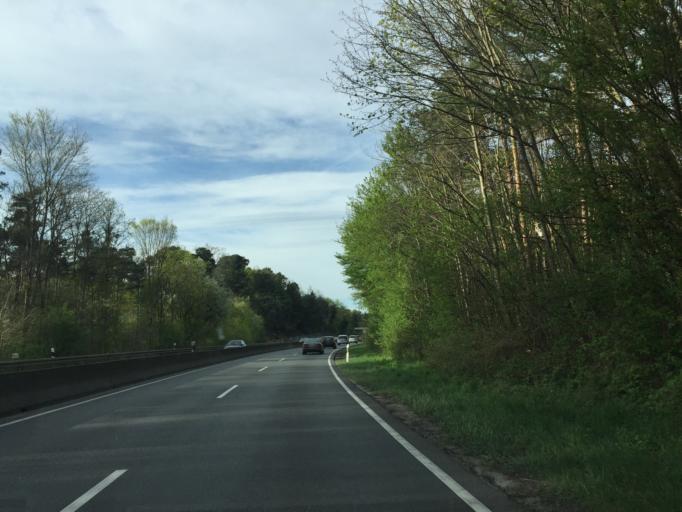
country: DE
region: Hesse
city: Pfungstadt
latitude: 49.8057
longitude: 8.6333
